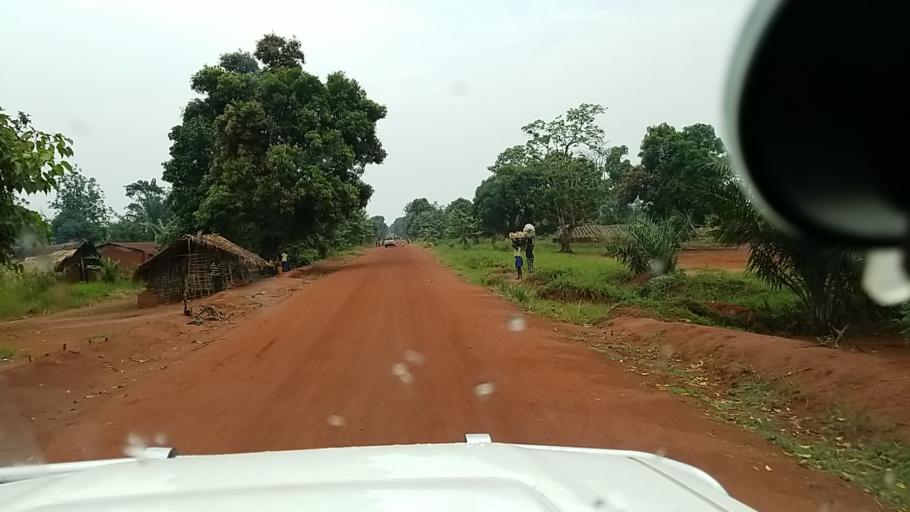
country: CD
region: Equateur
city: Gemena
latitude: 3.2183
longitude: 19.7823
